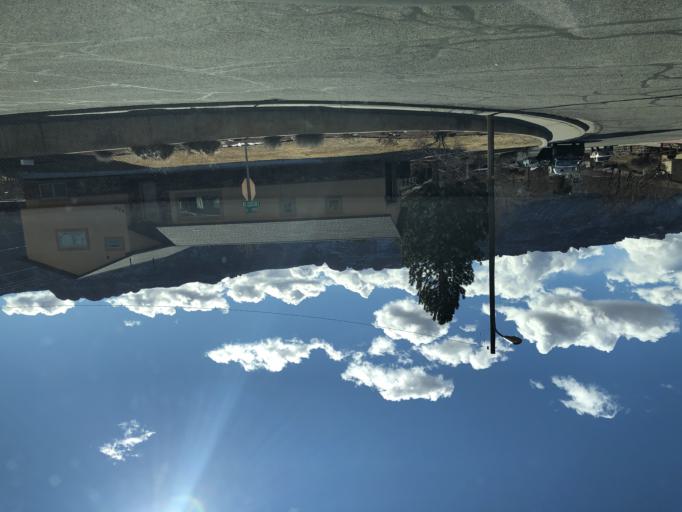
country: US
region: Utah
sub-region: Grand County
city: Moab
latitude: 38.5689
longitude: -109.5346
